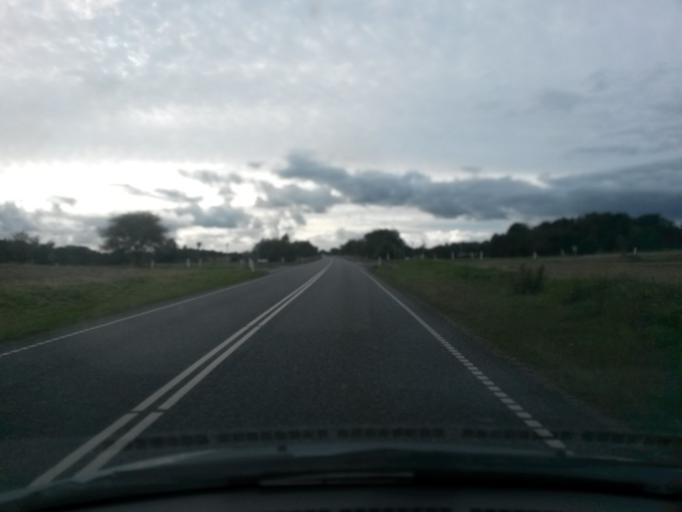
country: DK
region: Central Jutland
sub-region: Silkeborg Kommune
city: Kjellerup
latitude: 56.3001
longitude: 9.3637
